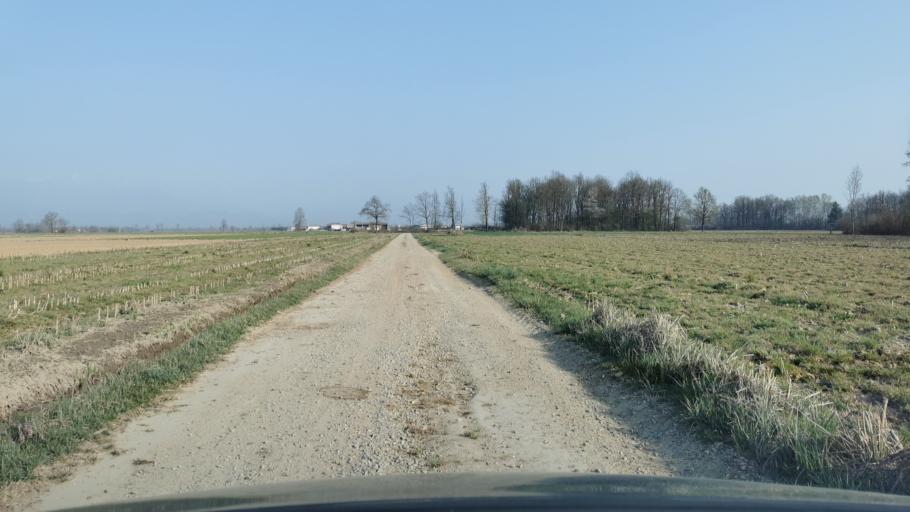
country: IT
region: Piedmont
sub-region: Provincia di Torino
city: Rivarossa
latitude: 45.2603
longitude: 7.7320
